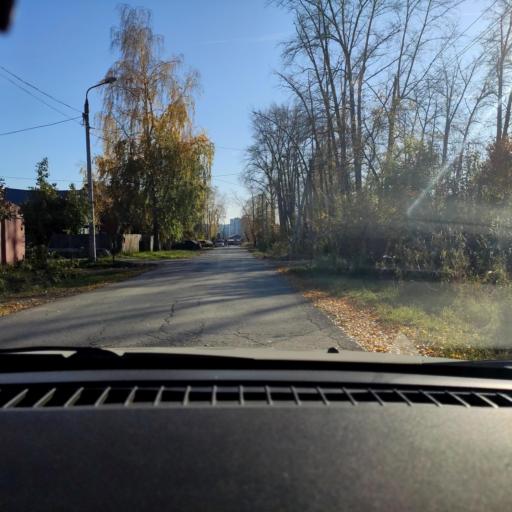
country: RU
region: Perm
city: Perm
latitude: 58.0790
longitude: 56.3572
